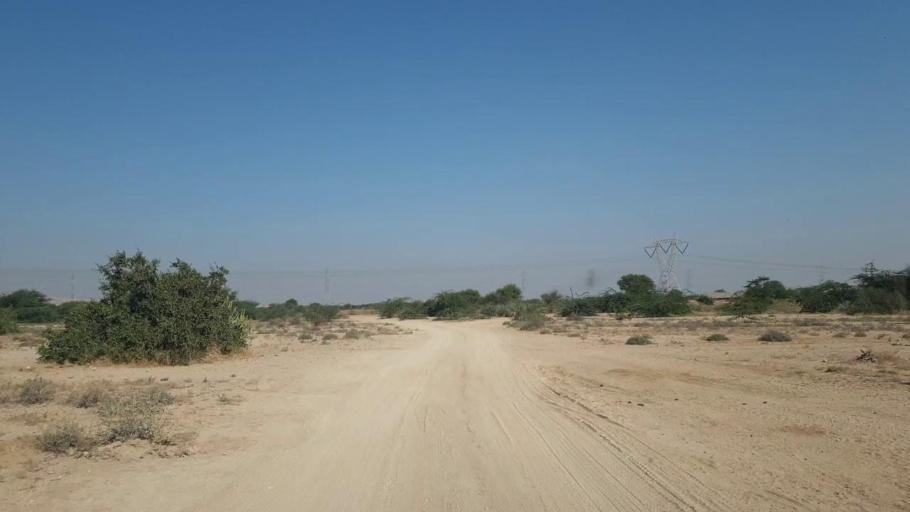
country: PK
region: Sindh
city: Gharo
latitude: 25.1866
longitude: 67.7380
